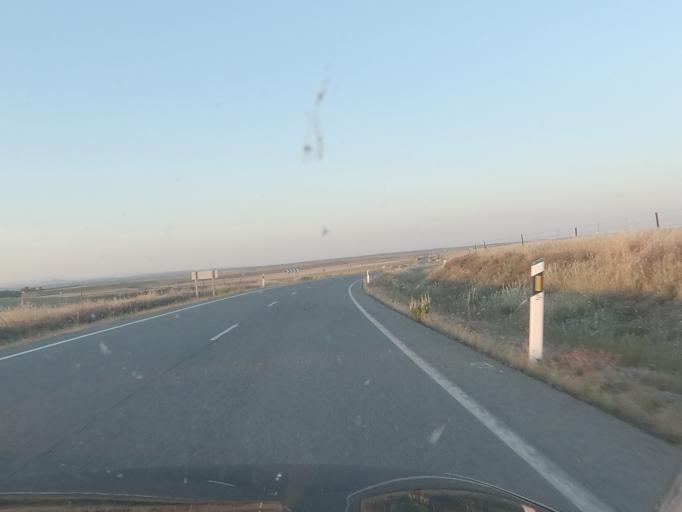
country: ES
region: Extremadura
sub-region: Provincia de Caceres
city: Alcantara
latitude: 39.6259
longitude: -6.9320
